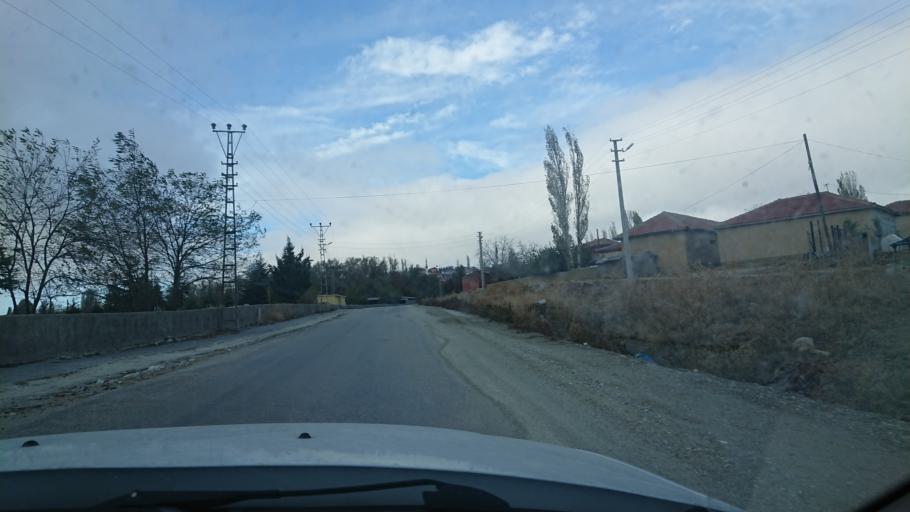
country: TR
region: Aksaray
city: Ortakoy
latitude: 38.7563
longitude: 34.0137
